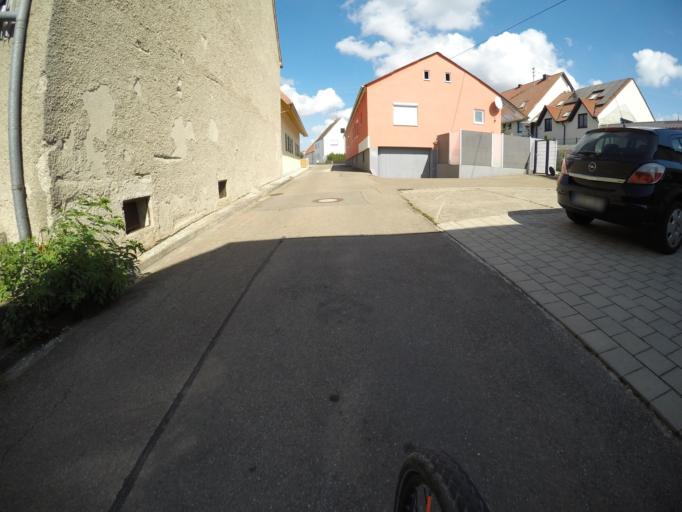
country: DE
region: Bavaria
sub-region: Swabia
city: Hochstadt an der Donau
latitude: 48.6181
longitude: 10.5366
